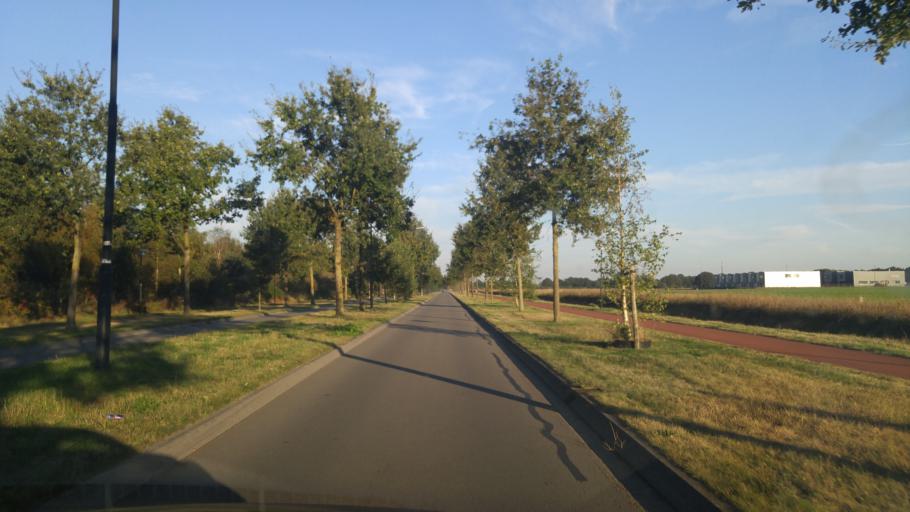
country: NL
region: North Brabant
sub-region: Gemeente Veldhoven
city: Oerle
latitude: 51.4345
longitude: 5.3643
